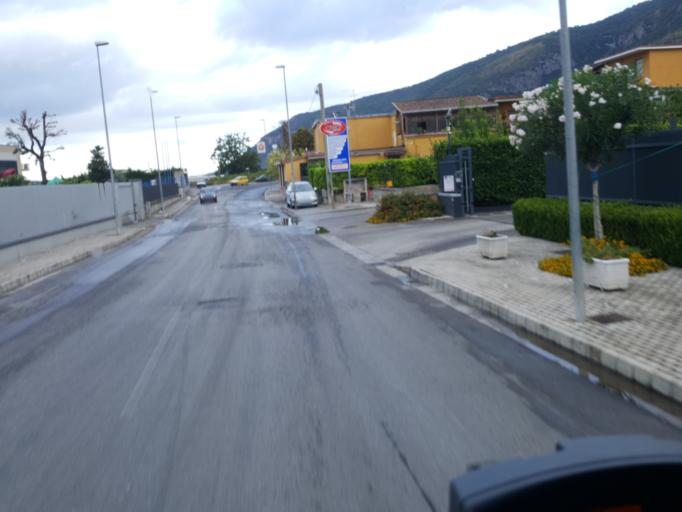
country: IT
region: Campania
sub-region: Provincia di Napoli
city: Striano
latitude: 40.8223
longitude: 14.5991
